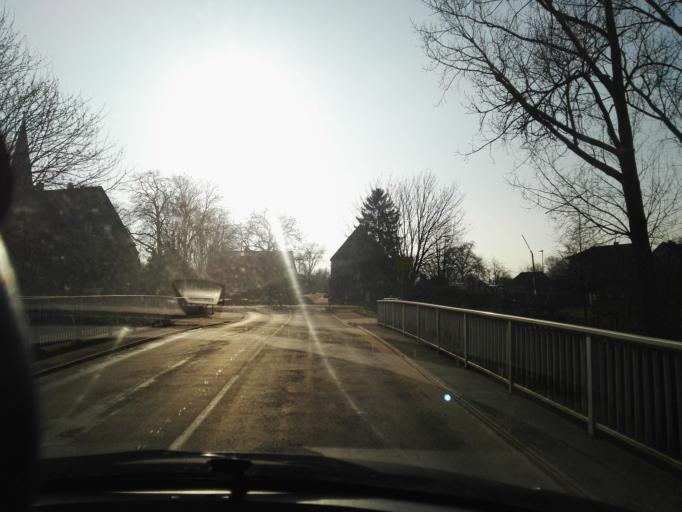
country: DE
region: Lower Saxony
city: Sarstedt
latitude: 52.2482
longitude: 9.8346
